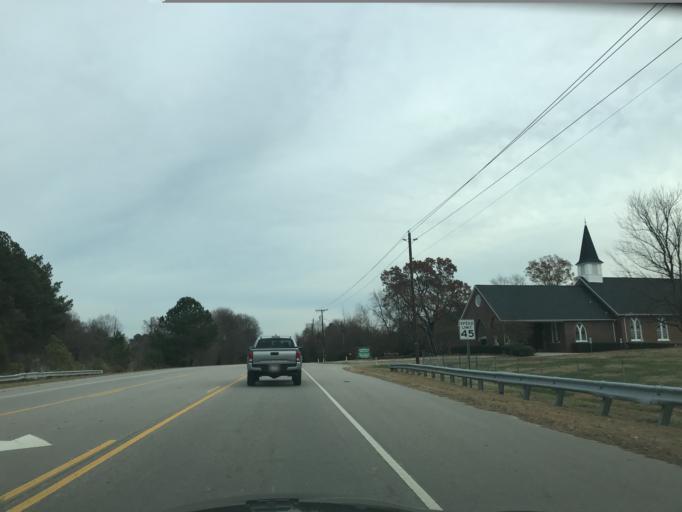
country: US
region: North Carolina
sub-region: Wake County
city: Cary
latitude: 35.7893
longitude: -78.7467
